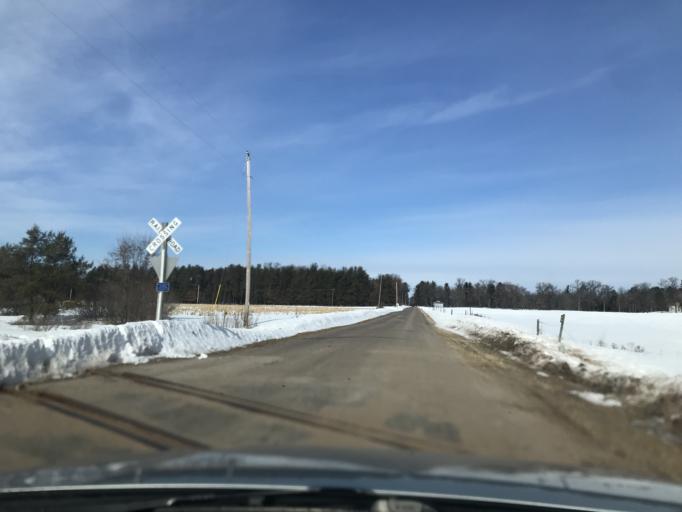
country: US
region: Wisconsin
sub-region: Marinette County
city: Peshtigo
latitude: 45.2184
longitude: -87.9627
